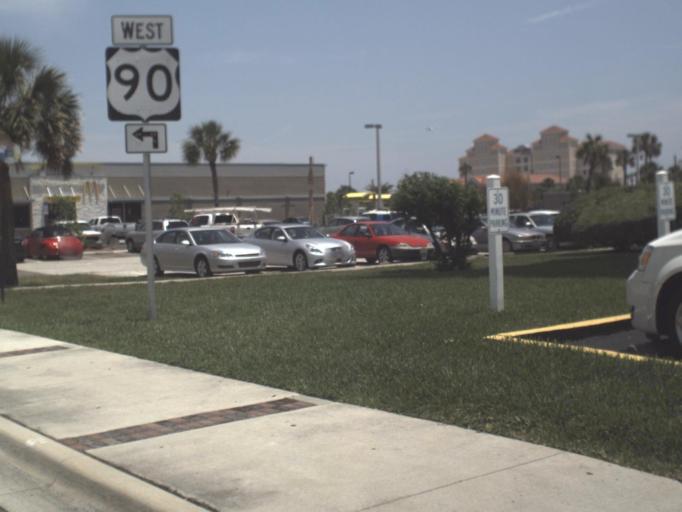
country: US
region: Florida
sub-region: Duval County
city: Jacksonville Beach
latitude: 30.2869
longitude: -81.3914
